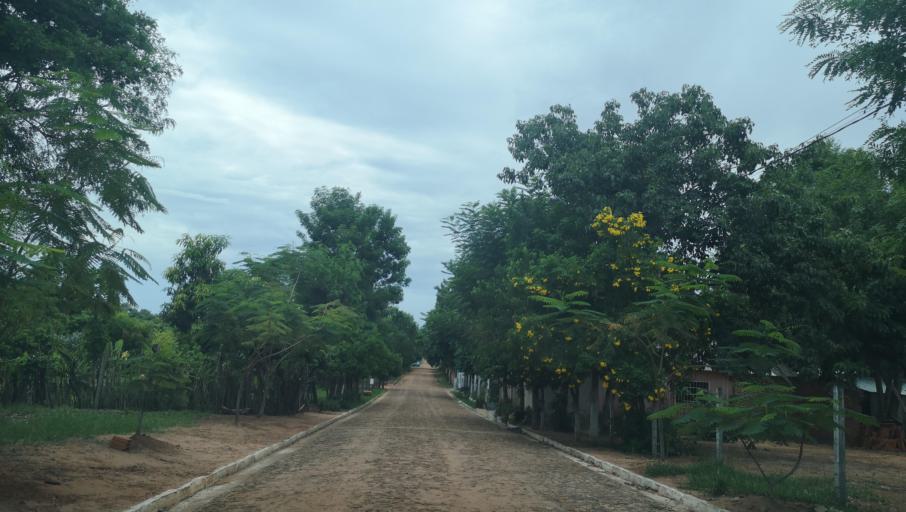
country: PY
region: San Pedro
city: Capiibary
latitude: -24.7318
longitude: -56.0159
